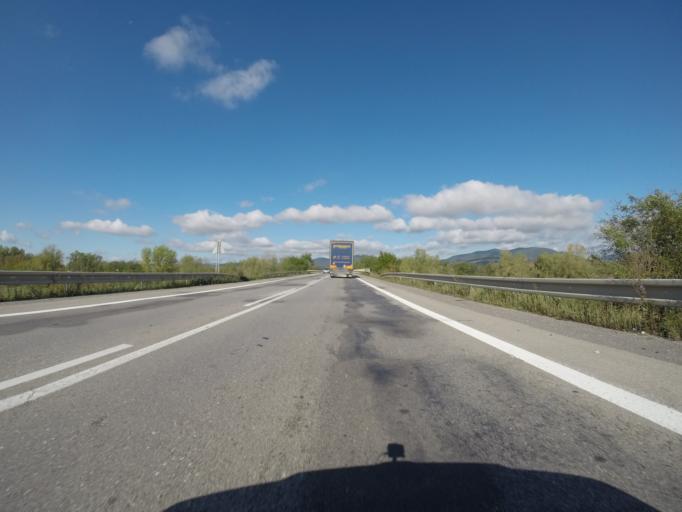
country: SK
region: Trenciansky
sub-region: Okres Trencin
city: Trencin
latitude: 48.8515
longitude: 17.9736
